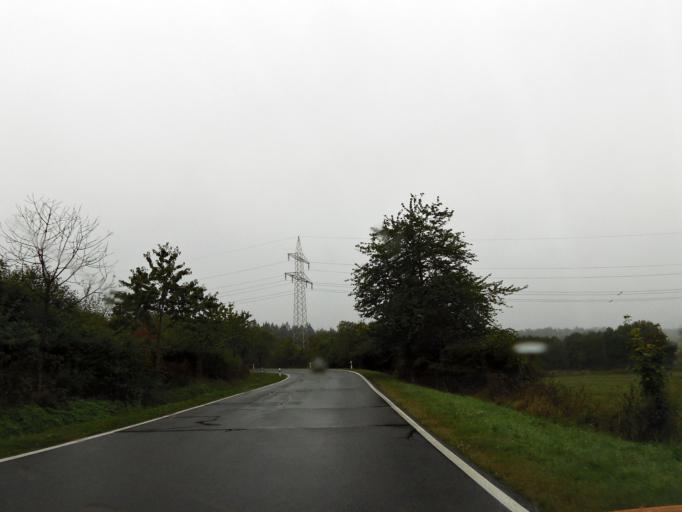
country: DE
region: Saxony-Anhalt
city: Hasselfelde
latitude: 51.6562
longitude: 10.8719
